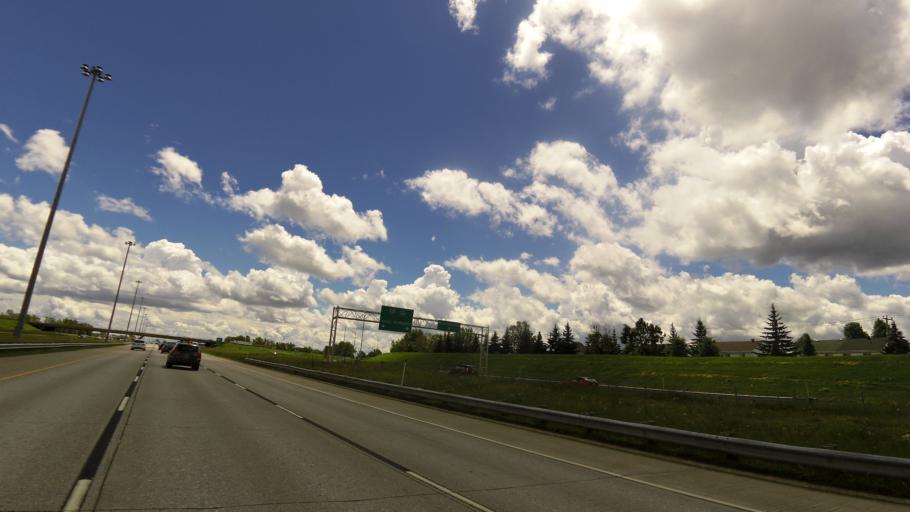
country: CA
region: Quebec
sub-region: Laurentides
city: Boisbriand
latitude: 45.5714
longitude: -73.8278
